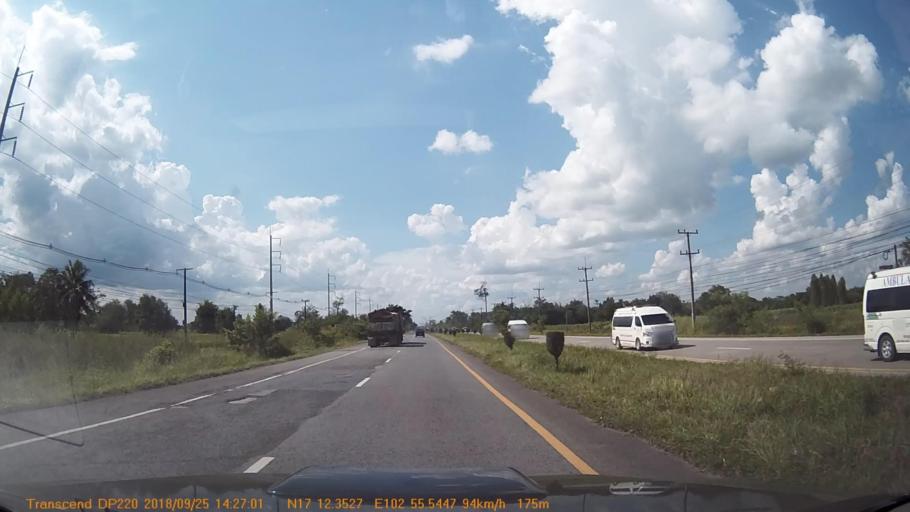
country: TH
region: Changwat Udon Thani
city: Ban Phan Don
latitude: 17.2061
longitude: 102.9256
